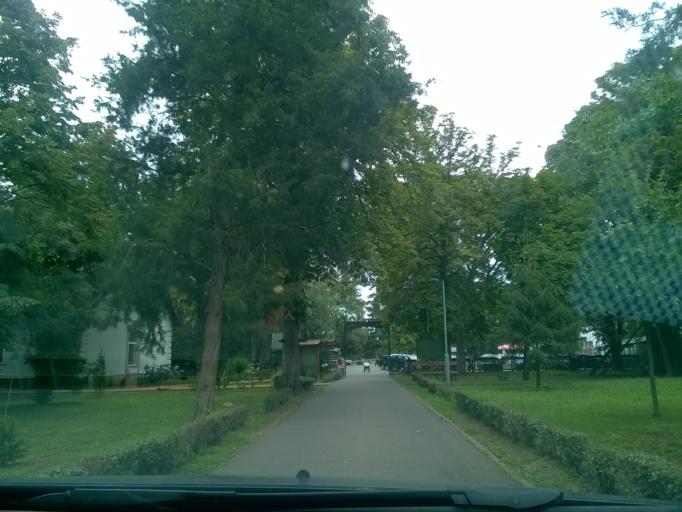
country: RS
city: Melenci
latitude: 45.5277
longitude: 20.3041
